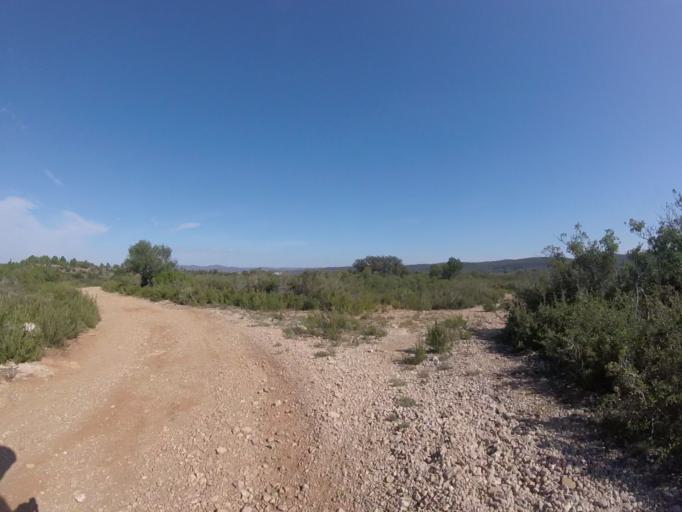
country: ES
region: Valencia
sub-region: Provincia de Castello
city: Cuevas de Vinroma
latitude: 40.2803
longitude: 0.0772
